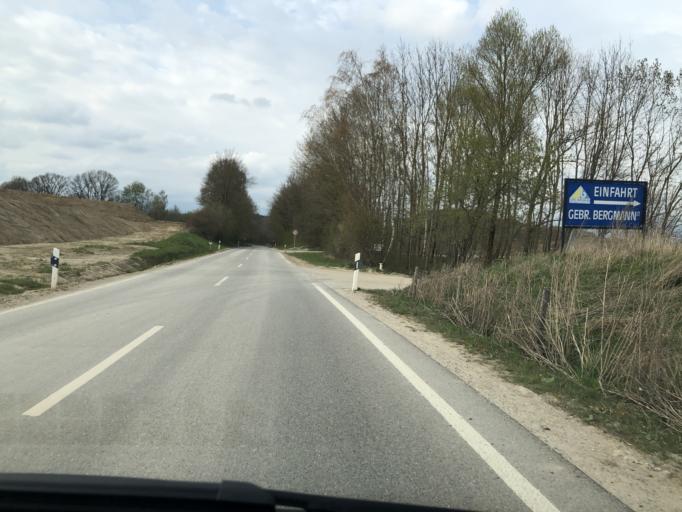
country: DE
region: Bavaria
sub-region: Upper Bavaria
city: Wolfersdorf
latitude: 48.5292
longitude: 11.6767
